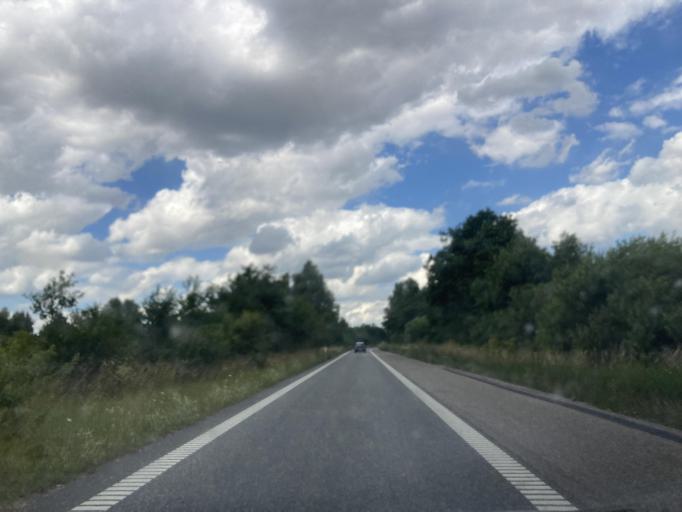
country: DK
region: Zealand
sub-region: Faxe Kommune
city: Haslev
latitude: 55.3411
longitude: 12.0490
